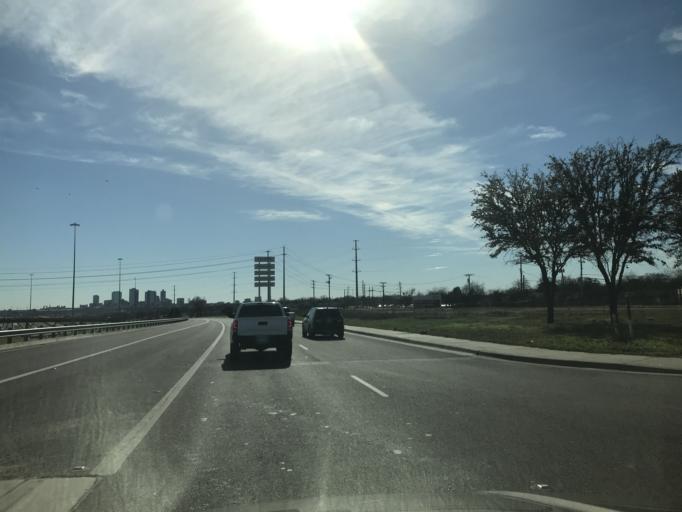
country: US
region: Texas
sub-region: Tarrant County
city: Haltom City
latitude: 32.7995
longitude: -97.3217
